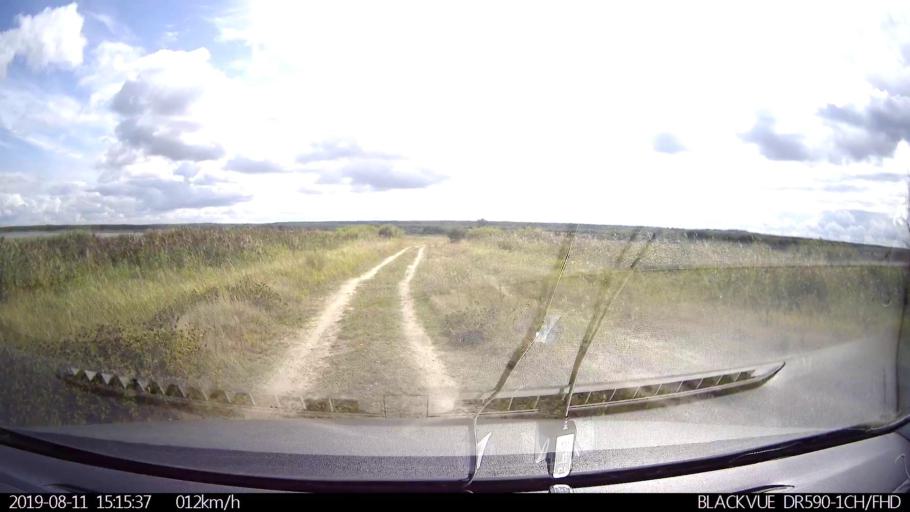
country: RU
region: Ulyanovsk
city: Ignatovka
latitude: 53.8487
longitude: 47.5893
